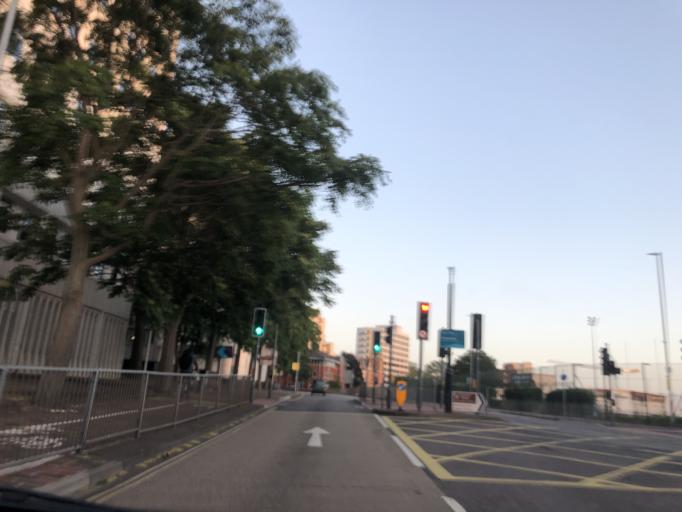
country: GB
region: England
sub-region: Portsmouth
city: Portsmouth
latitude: 50.7975
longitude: -1.0957
